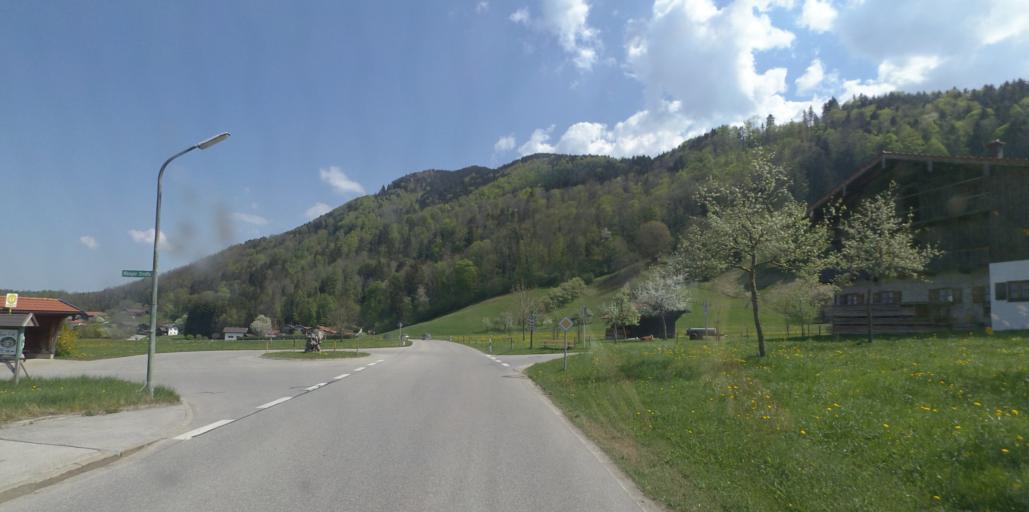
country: DE
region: Bavaria
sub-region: Upper Bavaria
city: Staudach-Egerndach
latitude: 47.7785
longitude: 12.4898
